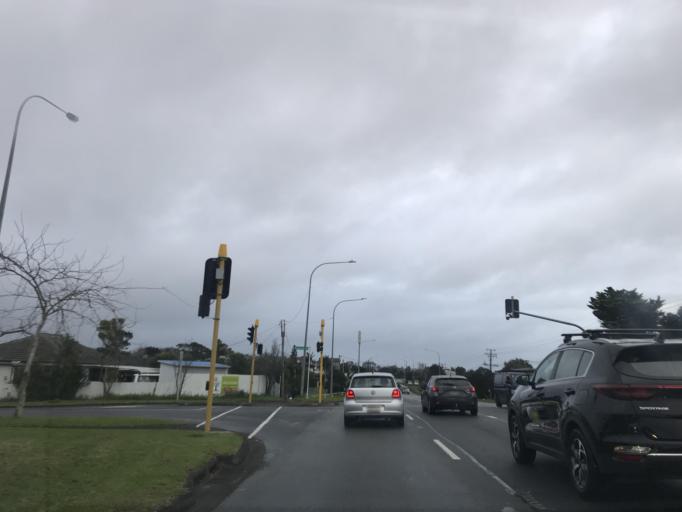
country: NZ
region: Auckland
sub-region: Auckland
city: Rothesay Bay
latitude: -36.7203
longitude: 174.7241
